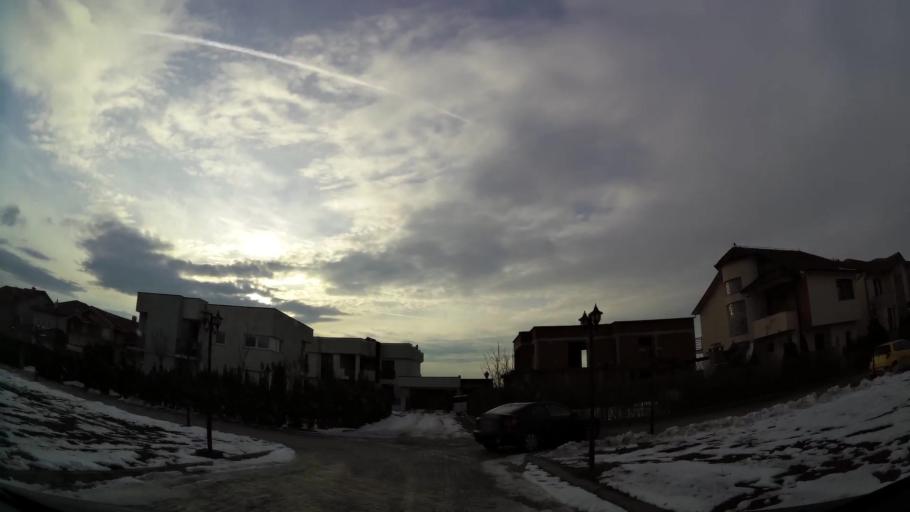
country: XK
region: Pristina
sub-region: Komuna e Prishtines
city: Pristina
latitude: 42.6242
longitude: 21.1603
